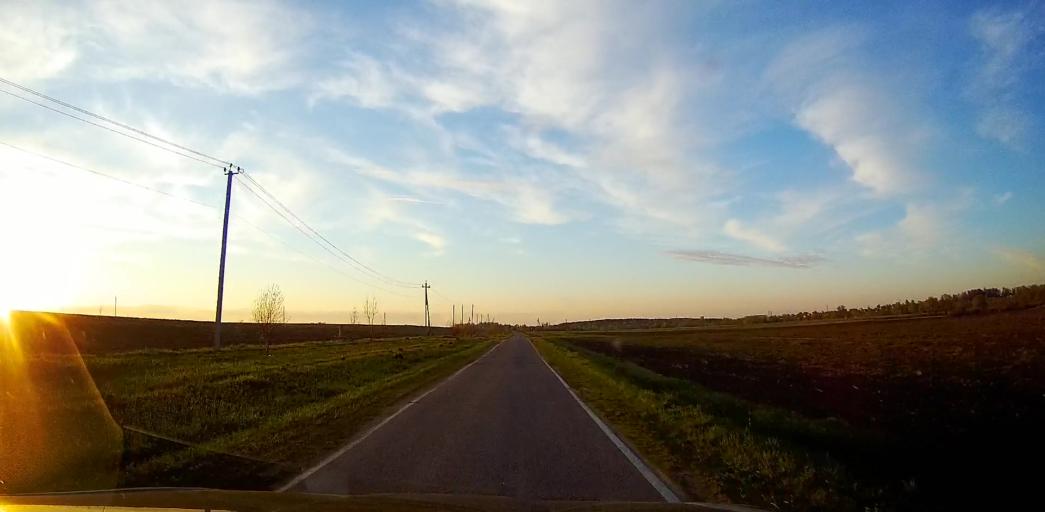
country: RU
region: Moskovskaya
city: Peski
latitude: 55.2165
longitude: 38.7386
